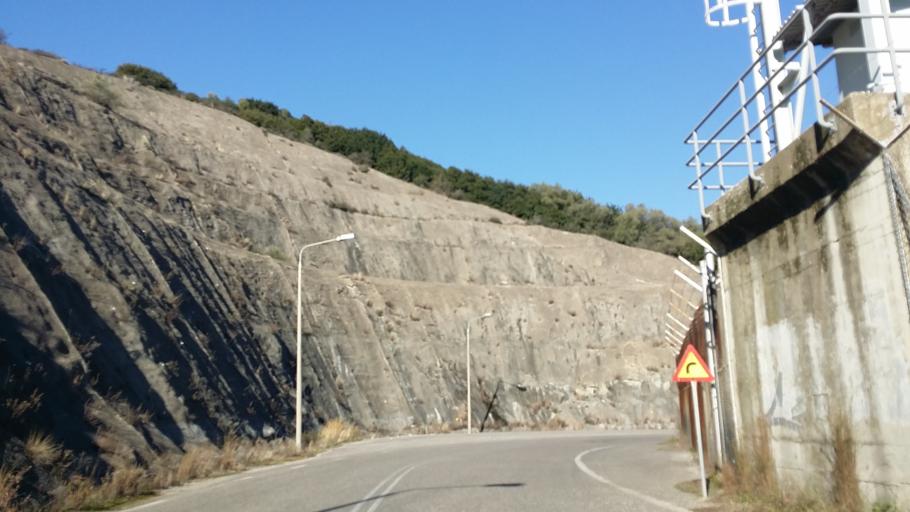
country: GR
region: West Greece
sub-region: Nomos Aitolias kai Akarnanias
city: Neapolis
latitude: 38.6773
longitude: 21.3238
